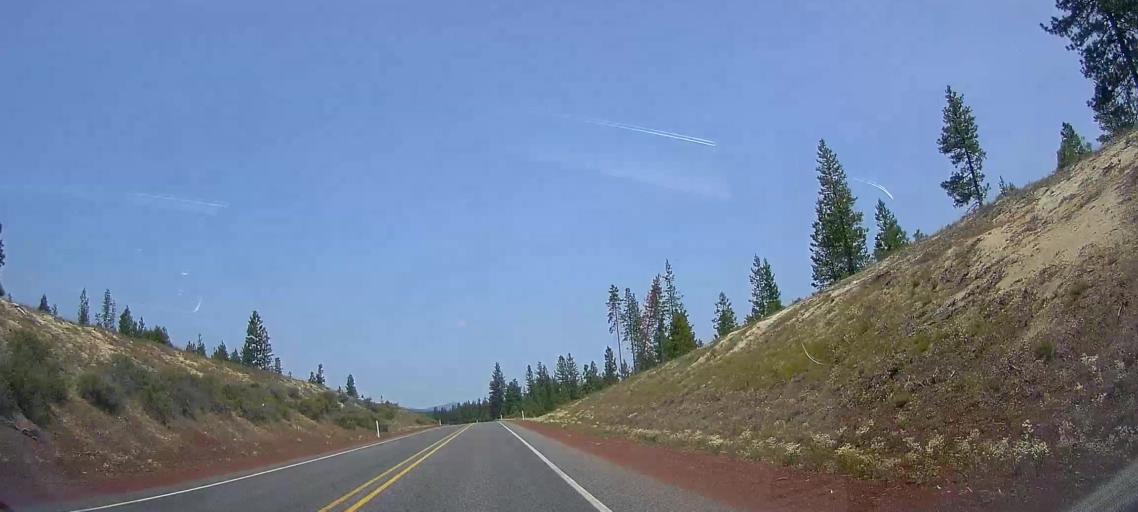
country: US
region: Oregon
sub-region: Deschutes County
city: La Pine
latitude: 43.4238
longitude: -121.7163
